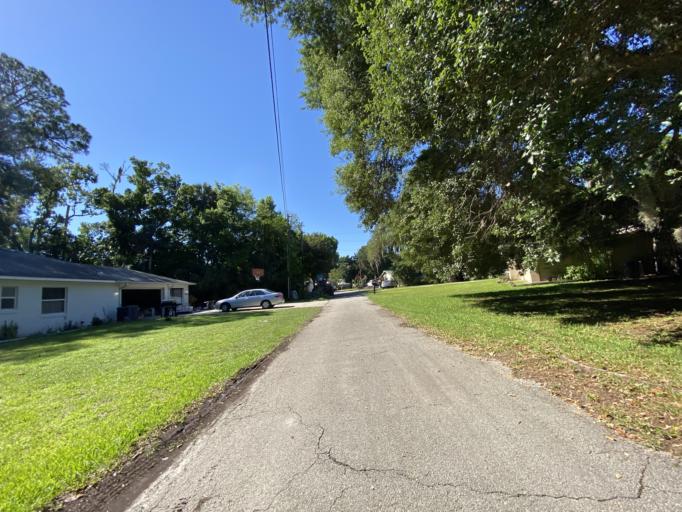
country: US
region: Florida
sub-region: Volusia County
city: Port Orange
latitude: 29.1429
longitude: -81.0021
